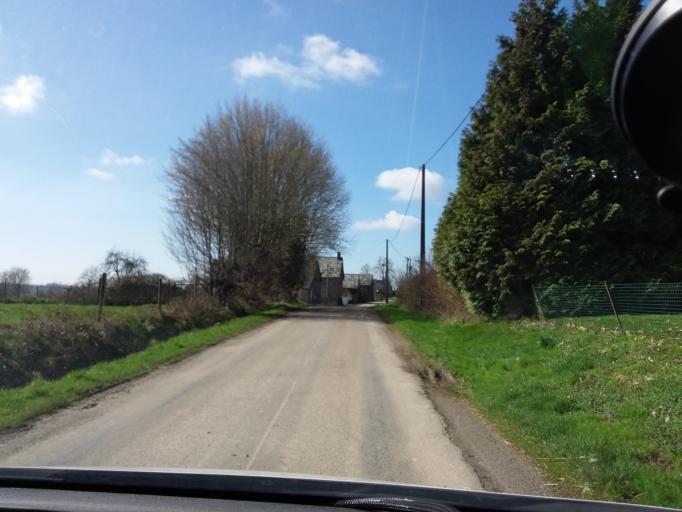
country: FR
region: Picardie
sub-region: Departement de l'Aisne
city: Origny-en-Thierache
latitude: 49.8261
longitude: 4.0438
